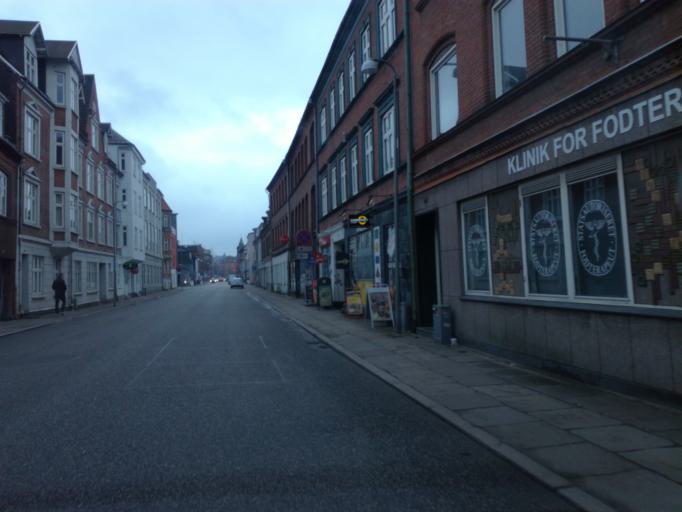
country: DK
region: South Denmark
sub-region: Vejle Kommune
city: Vejle
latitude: 55.7135
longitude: 9.5336
